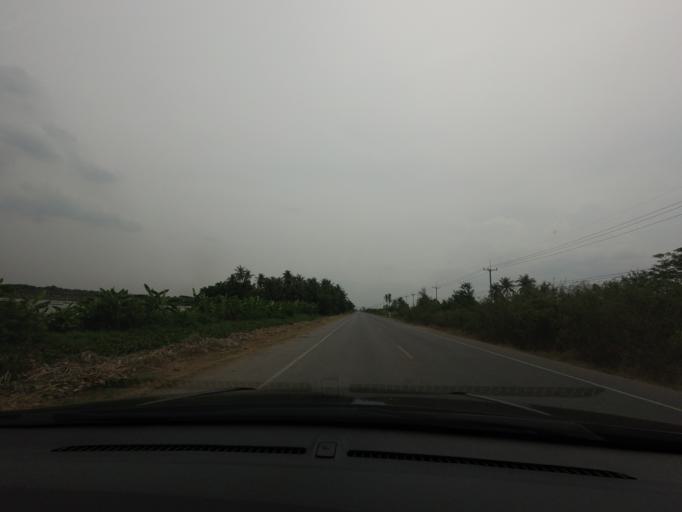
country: TH
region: Phetchaburi
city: Ban Laem
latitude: 13.1793
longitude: 99.9399
